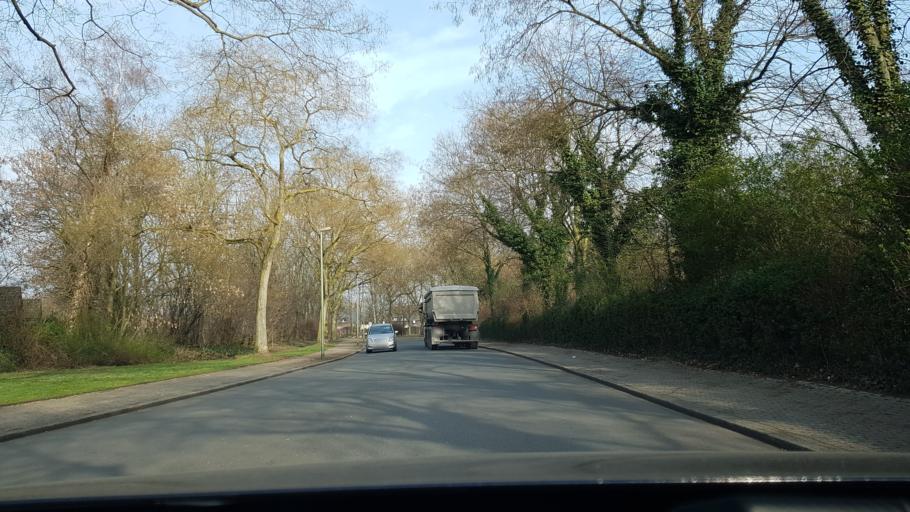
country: DE
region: North Rhine-Westphalia
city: Meiderich
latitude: 51.4935
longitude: 6.7919
